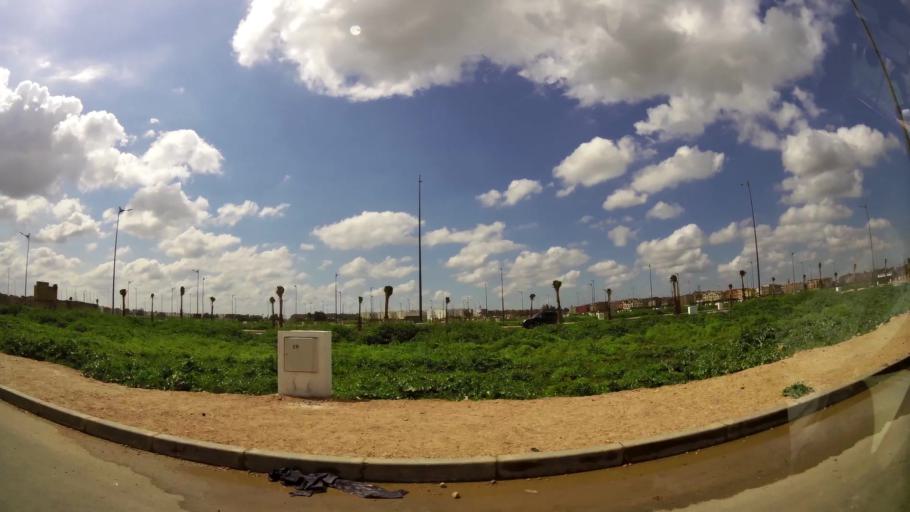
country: MA
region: Grand Casablanca
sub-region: Mediouna
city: Mediouna
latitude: 33.3659
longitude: -7.5327
